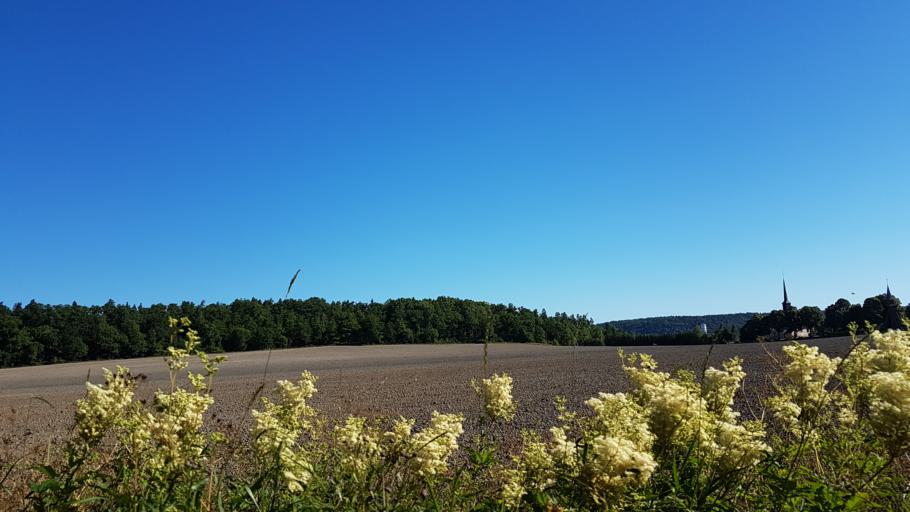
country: SE
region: OEstergoetland
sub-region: Valdemarsviks Kommun
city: Gusum
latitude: 58.4285
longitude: 16.5834
